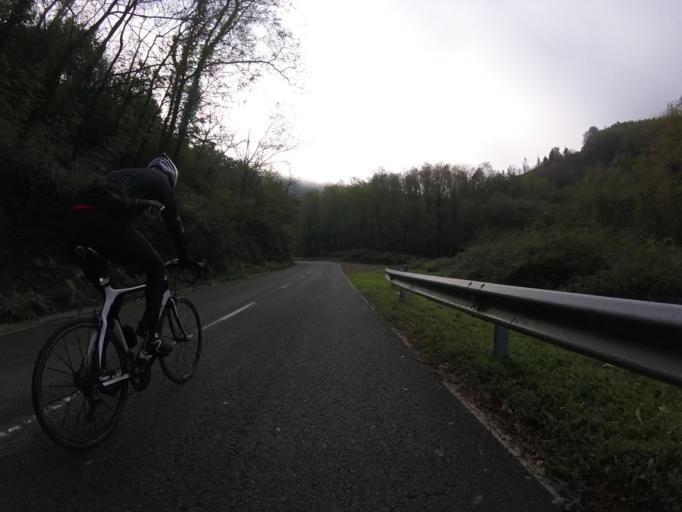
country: ES
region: Navarre
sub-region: Provincia de Navarra
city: Arano
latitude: 43.2055
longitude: -1.8811
